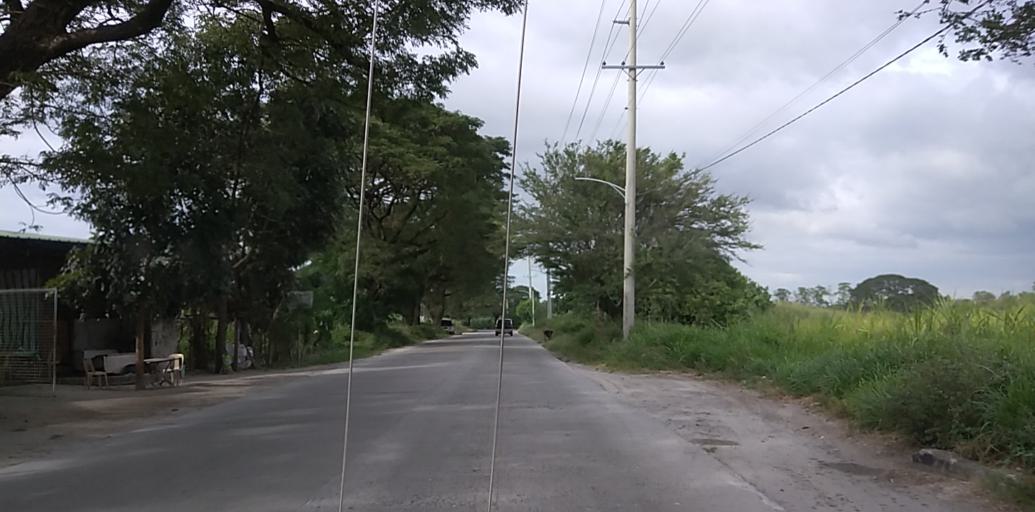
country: PH
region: Central Luzon
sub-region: Province of Pampanga
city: Porac
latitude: 15.0761
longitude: 120.5495
